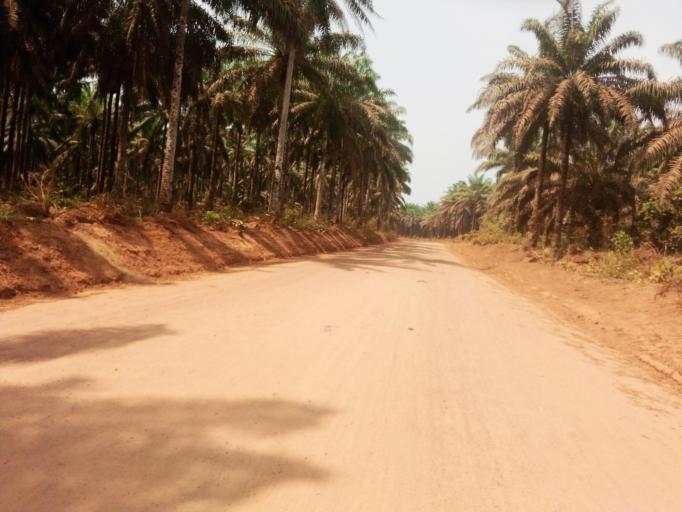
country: SL
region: Southern Province
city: Sumbuya
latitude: 7.6201
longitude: -12.1220
